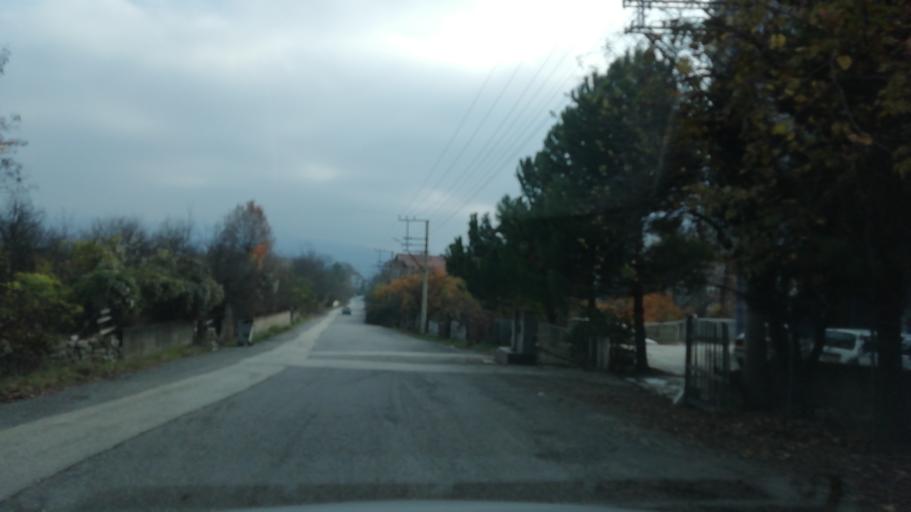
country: TR
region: Karabuk
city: Karabuk
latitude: 41.2252
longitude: 32.6234
